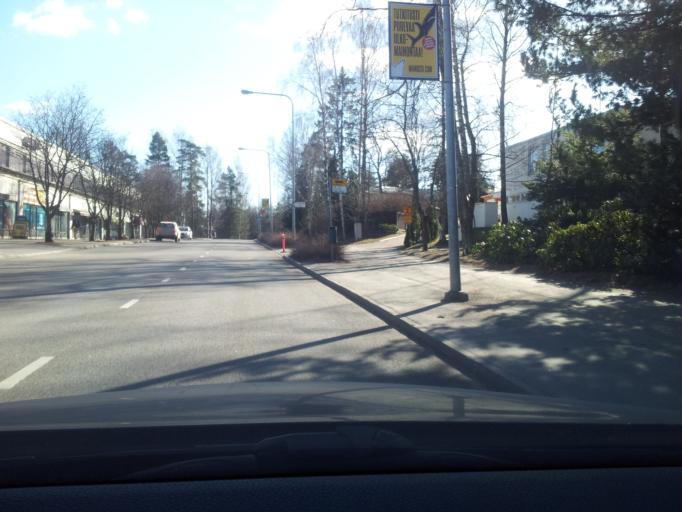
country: FI
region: Uusimaa
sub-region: Helsinki
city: Koukkuniemi
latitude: 60.1637
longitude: 24.7903
